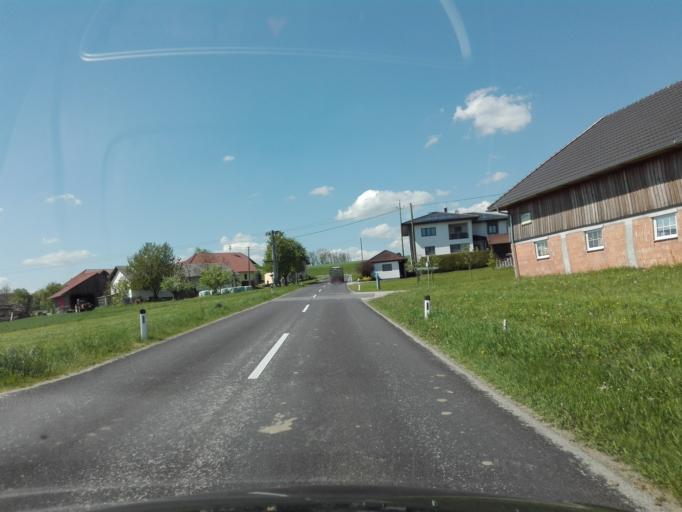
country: AT
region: Upper Austria
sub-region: Politischer Bezirk Urfahr-Umgebung
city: Feldkirchen an der Donau
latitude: 48.3500
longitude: 13.9447
